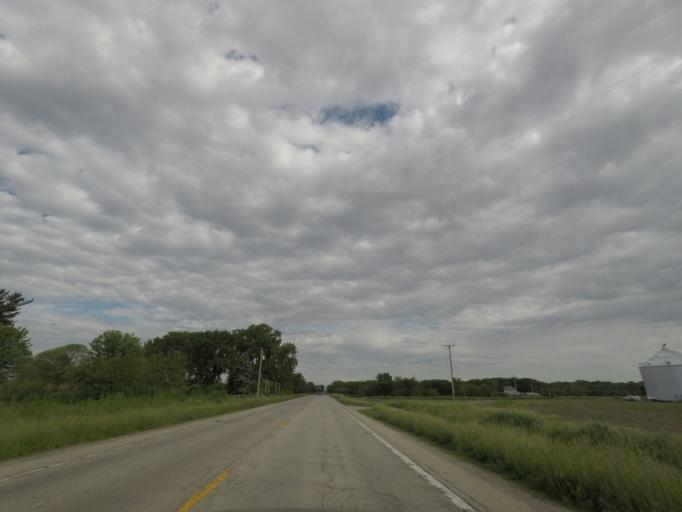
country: US
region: Illinois
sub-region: Logan County
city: Lincoln
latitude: 40.1132
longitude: -89.3297
